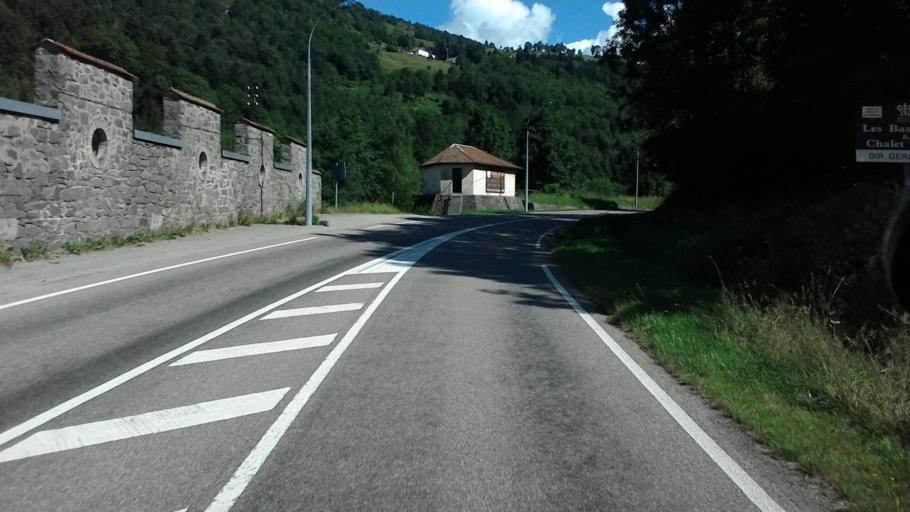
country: FR
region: Lorraine
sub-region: Departement des Vosges
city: Cornimont
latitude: 47.9813
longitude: 6.8339
